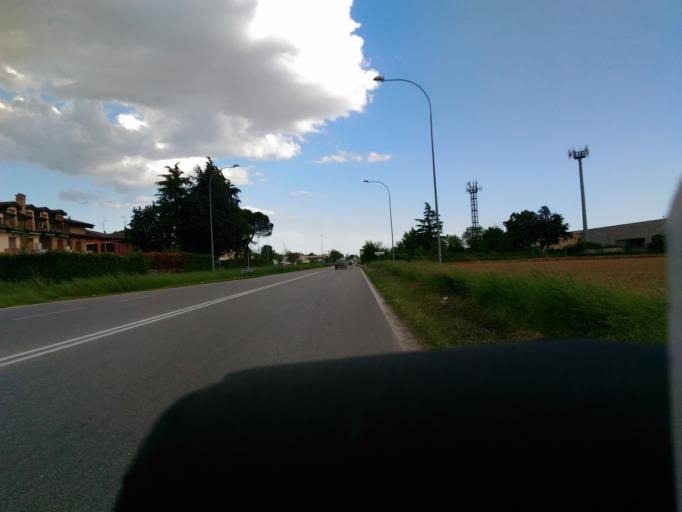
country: IT
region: Lombardy
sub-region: Citta metropolitana di Milano
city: Mediglia
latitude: 45.3961
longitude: 9.3266
